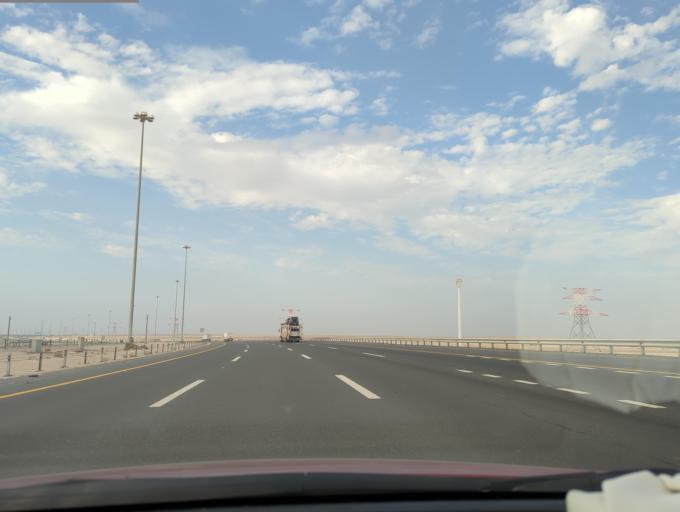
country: AE
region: Abu Dhabi
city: Abu Dhabi
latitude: 24.4312
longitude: 54.7657
